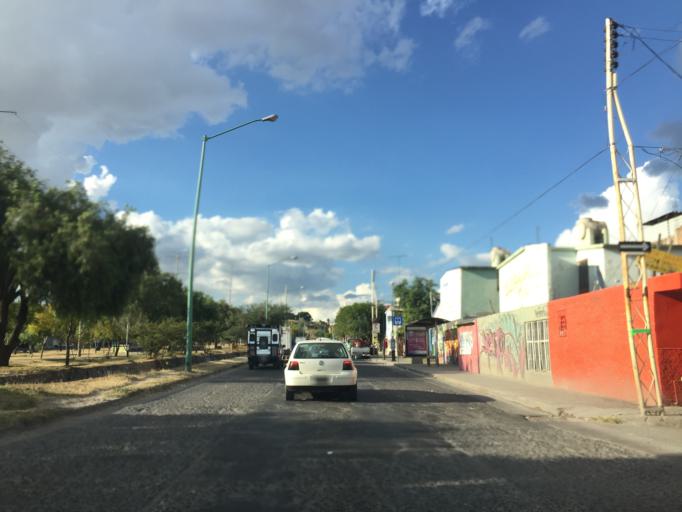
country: MX
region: Guanajuato
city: Leon
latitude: 21.1032
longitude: -101.7103
